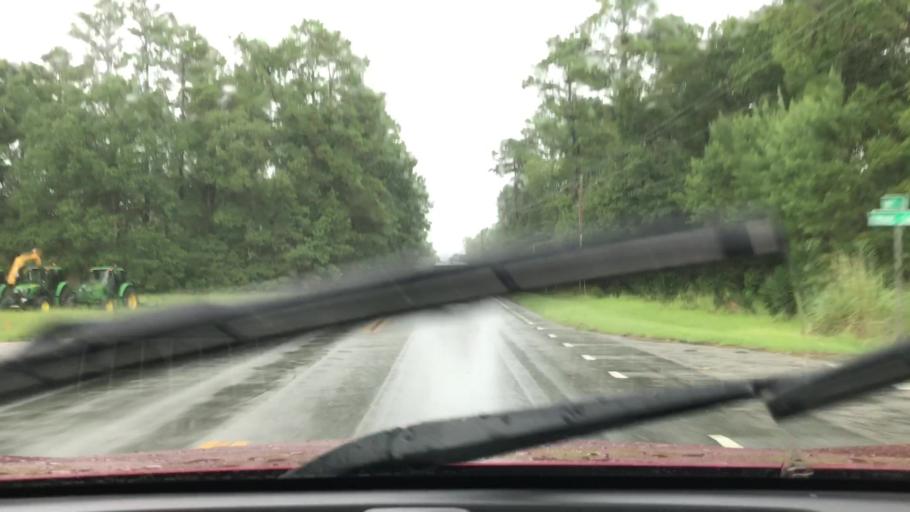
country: US
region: South Carolina
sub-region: Horry County
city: Socastee
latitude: 33.7277
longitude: -79.0843
